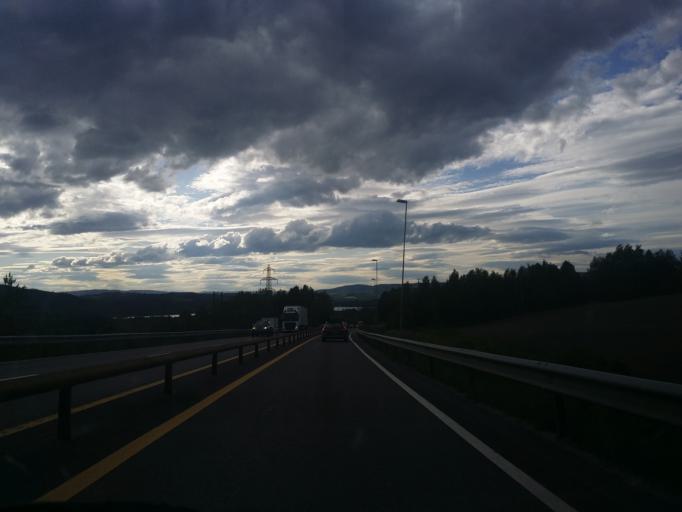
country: NO
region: Hedmark
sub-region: Ringsaker
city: Brumunddal
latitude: 60.8556
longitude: 10.9824
